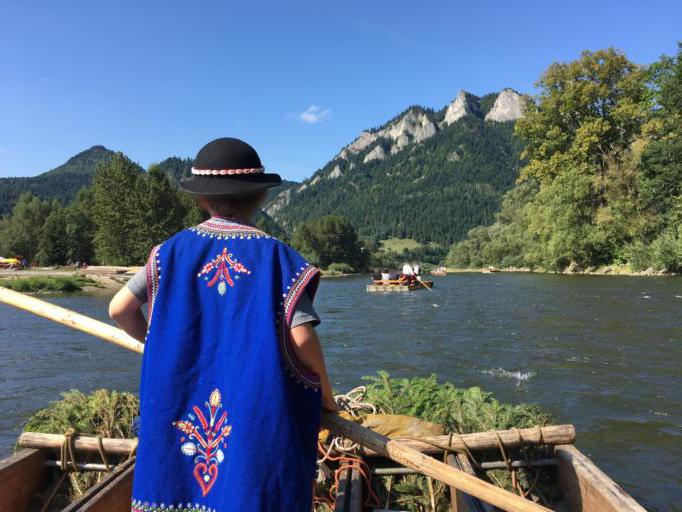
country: PL
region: Lesser Poland Voivodeship
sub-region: Powiat nowotarski
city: Kroscienko nad Dunajcem
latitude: 49.3981
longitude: 20.4147
